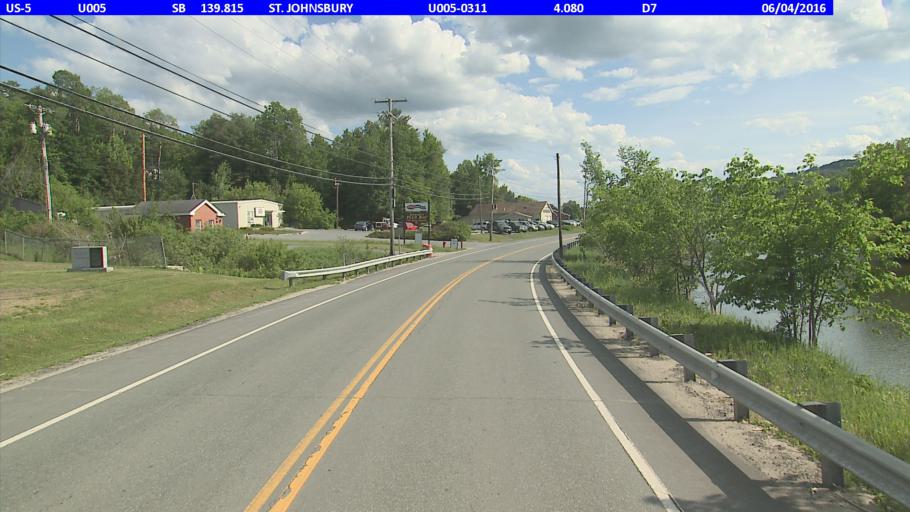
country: US
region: Vermont
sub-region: Caledonia County
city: St Johnsbury
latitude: 44.4501
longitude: -72.0156
